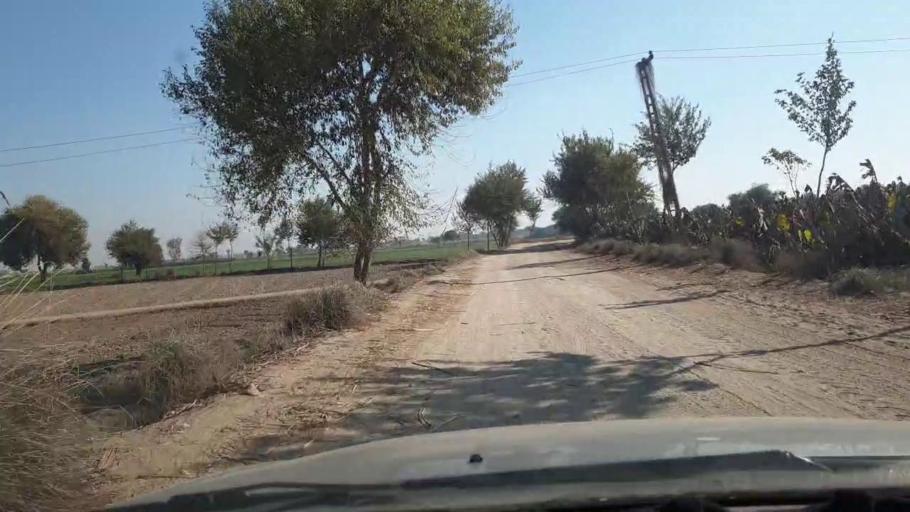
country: PK
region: Sindh
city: Ghotki
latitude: 28.0225
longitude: 69.2217
